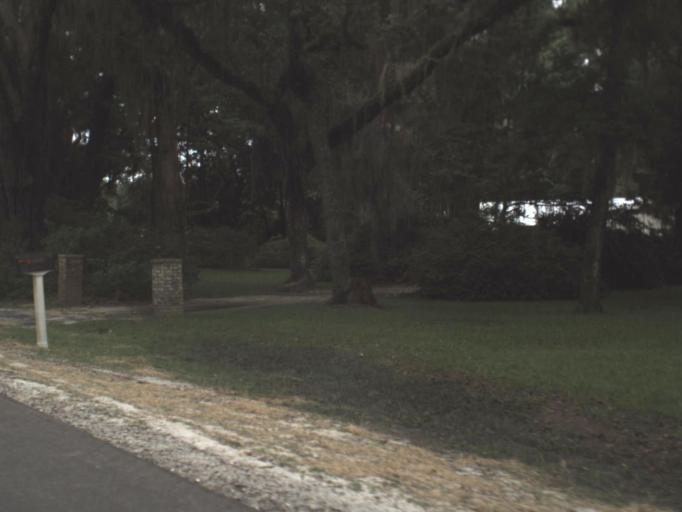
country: US
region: Florida
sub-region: Alachua County
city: Archer
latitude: 29.5134
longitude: -82.5087
